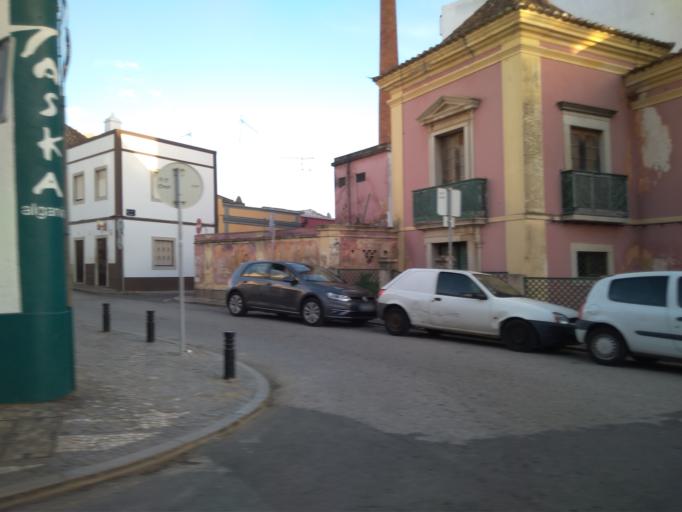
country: PT
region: Faro
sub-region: Faro
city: Faro
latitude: 37.0189
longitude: -7.9336
